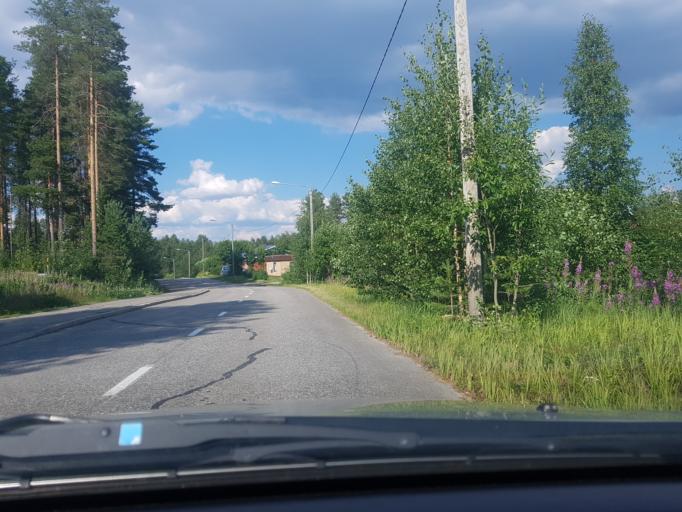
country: FI
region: Kainuu
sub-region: Kehys-Kainuu
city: Kuhmo
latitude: 64.1286
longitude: 29.5426
